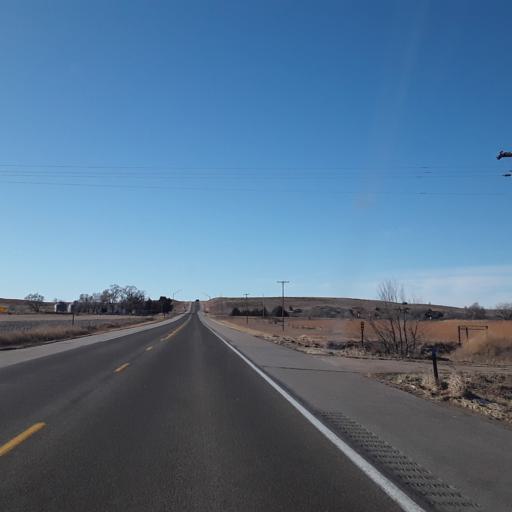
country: US
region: Nebraska
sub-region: Hitchcock County
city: Trenton
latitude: 40.2344
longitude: -100.8903
